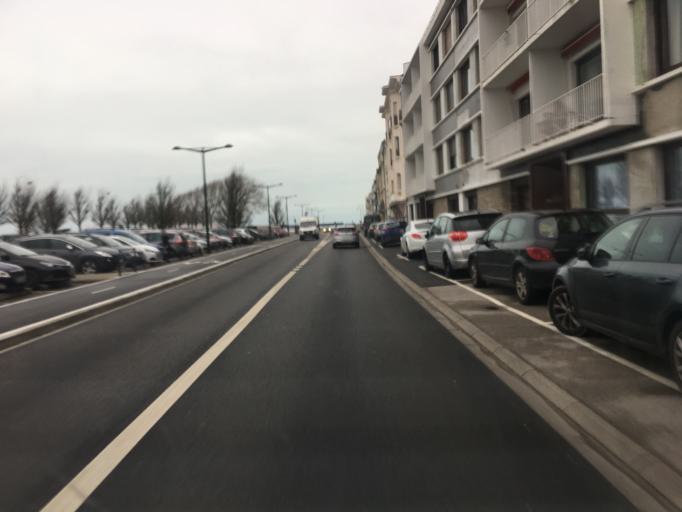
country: FR
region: Nord-Pas-de-Calais
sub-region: Departement du Pas-de-Calais
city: Saint-Martin-Boulogne
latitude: 50.7329
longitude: 1.5951
